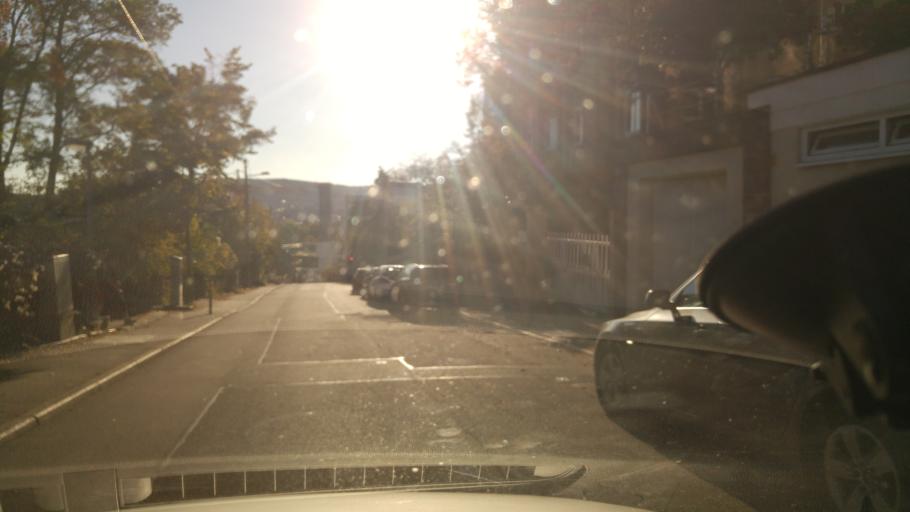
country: DE
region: Baden-Wuerttemberg
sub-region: Regierungsbezirk Stuttgart
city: Stuttgart
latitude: 48.7859
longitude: 9.1738
